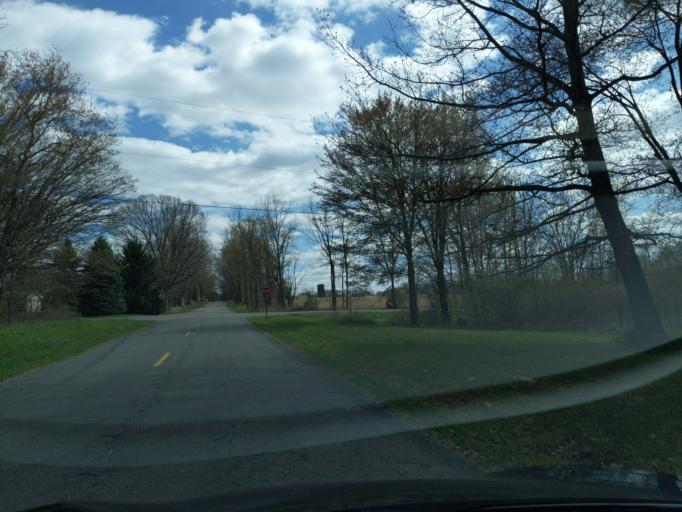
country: US
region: Michigan
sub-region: Ingham County
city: Leslie
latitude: 42.4371
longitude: -84.5263
